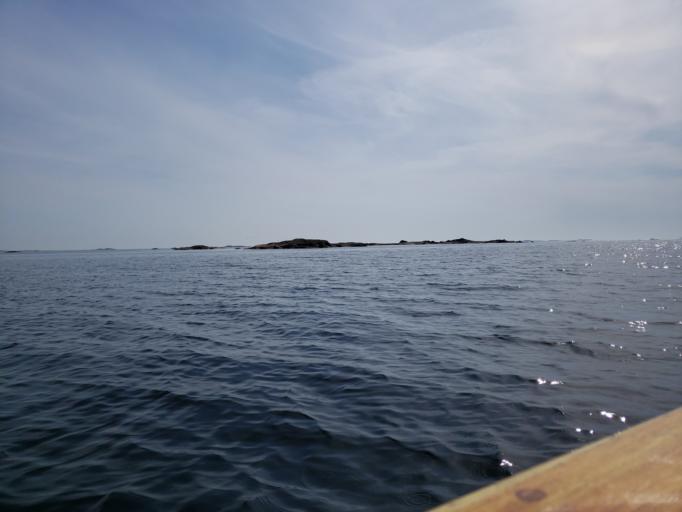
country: FI
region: Varsinais-Suomi
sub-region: Aboland-Turunmaa
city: Dragsfjaerd
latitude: 59.8386
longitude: 22.2003
